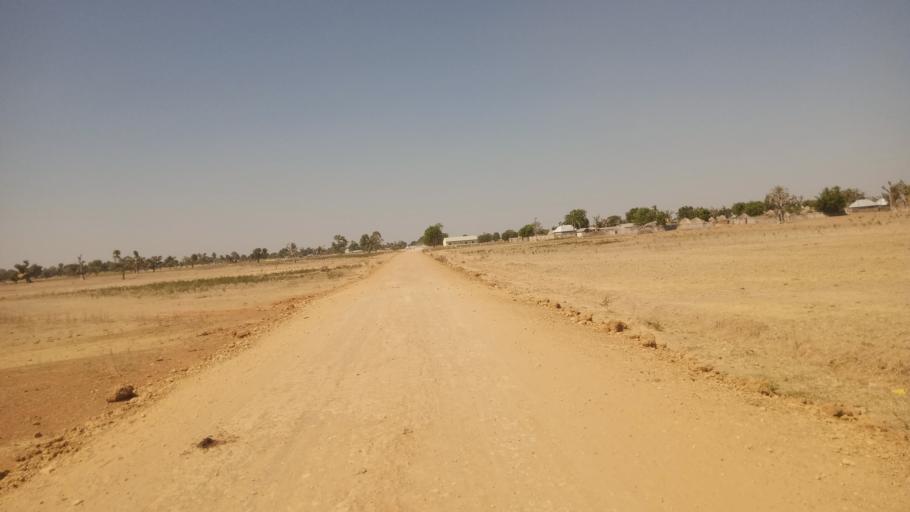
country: NG
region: Adamawa
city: Ngurore
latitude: 9.2976
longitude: 12.1430
